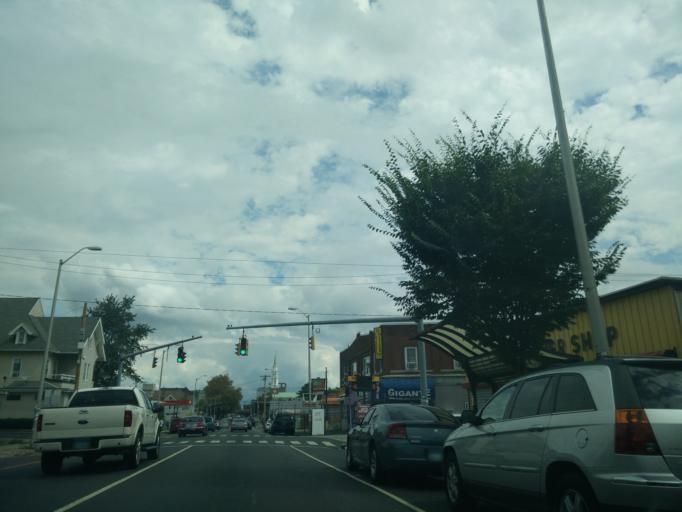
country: US
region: Connecticut
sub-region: Fairfield County
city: Bridgeport
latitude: 41.1723
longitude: -73.2030
